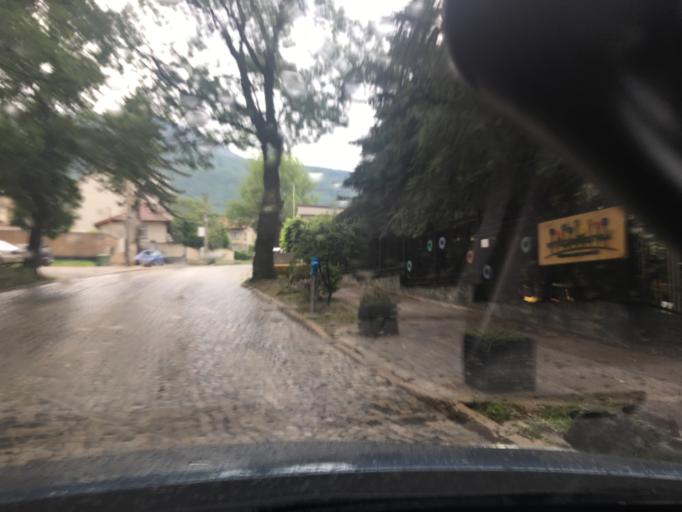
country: BG
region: Sofia-Capital
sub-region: Stolichna Obshtina
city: Sofia
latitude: 42.6295
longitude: 23.3129
